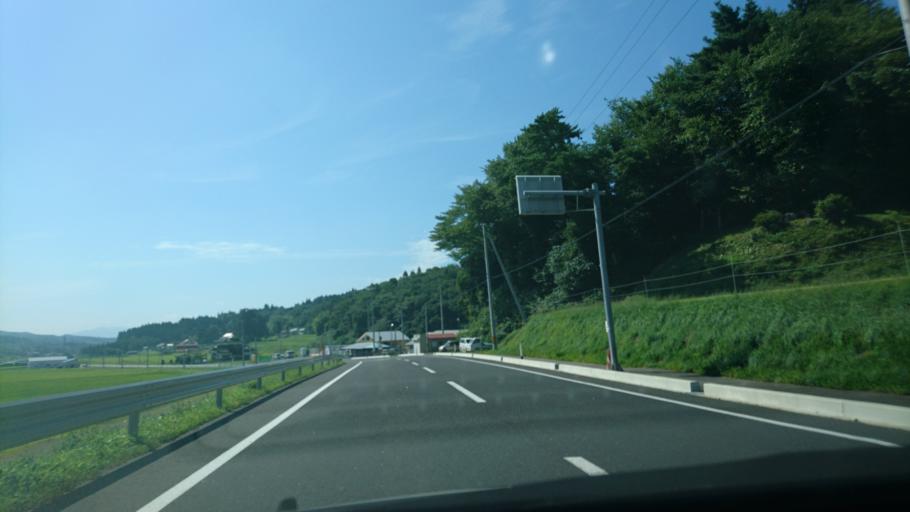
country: JP
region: Iwate
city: Ofunato
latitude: 39.0150
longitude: 141.4216
